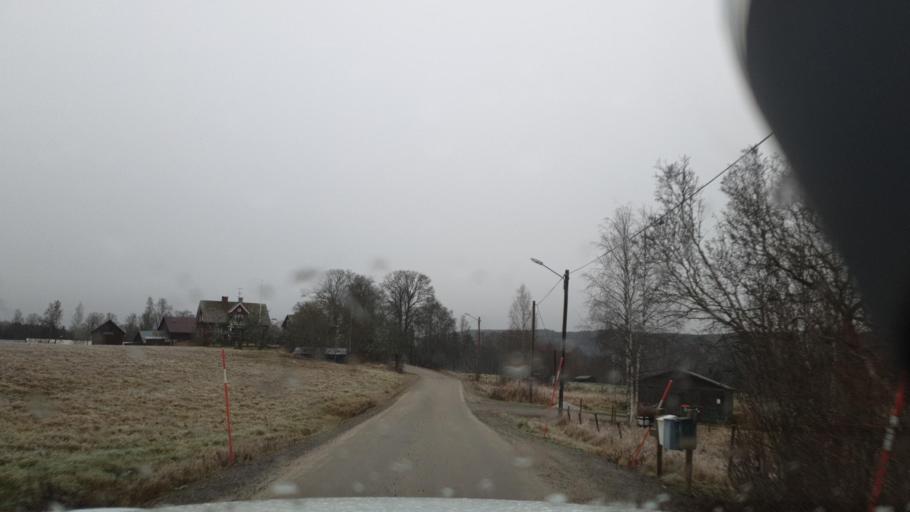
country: SE
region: Vaermland
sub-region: Arvika Kommun
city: Arvika
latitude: 59.6698
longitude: 12.7681
